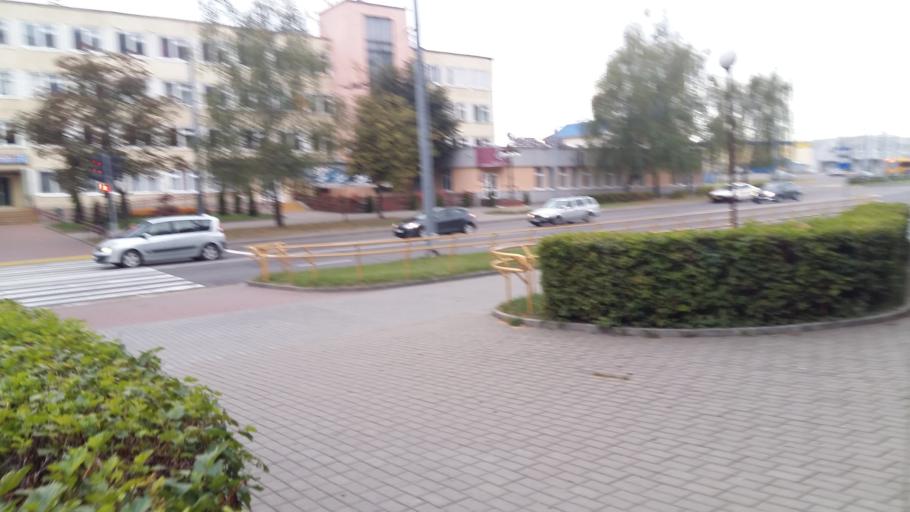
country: BY
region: Grodnenskaya
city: Hrodna
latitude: 53.7111
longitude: 23.8402
